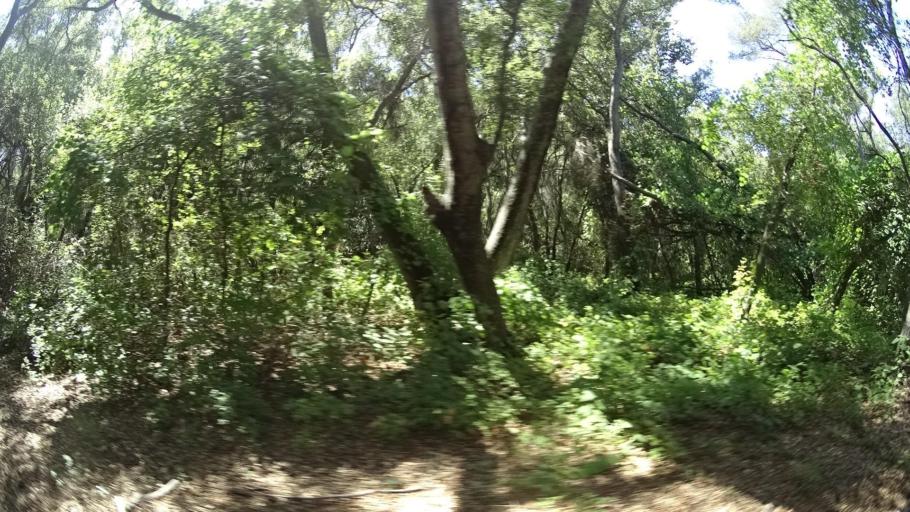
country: US
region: California
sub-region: San Diego County
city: Rainbow
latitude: 33.3413
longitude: -117.0811
